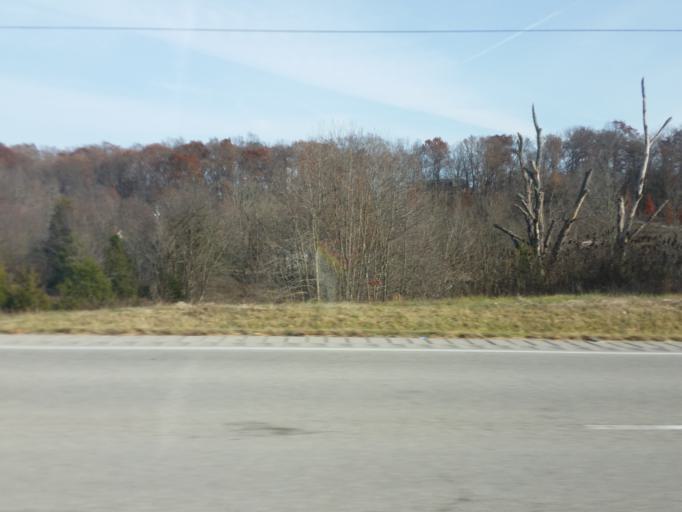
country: US
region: Kentucky
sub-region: Harrison County
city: Cynthiana
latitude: 38.5103
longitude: -84.2923
